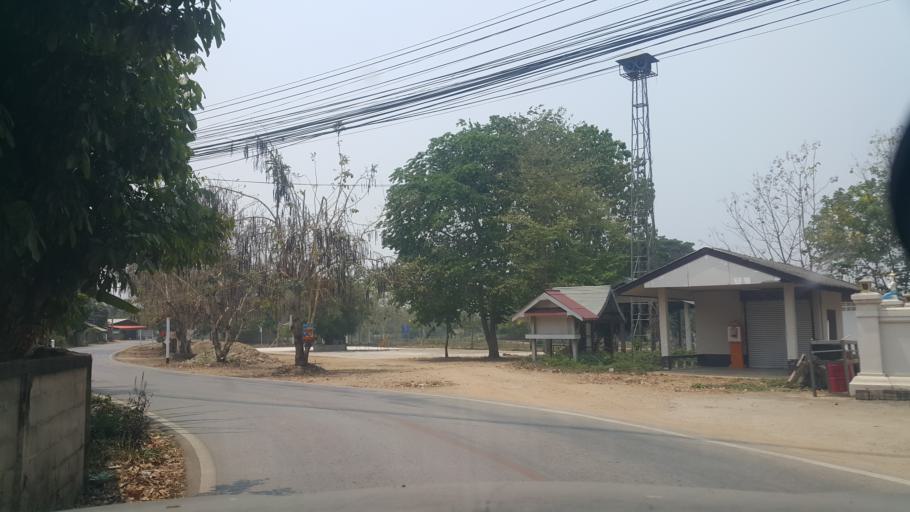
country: TH
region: Lampang
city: Soem Ngam
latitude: 18.0720
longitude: 99.2289
